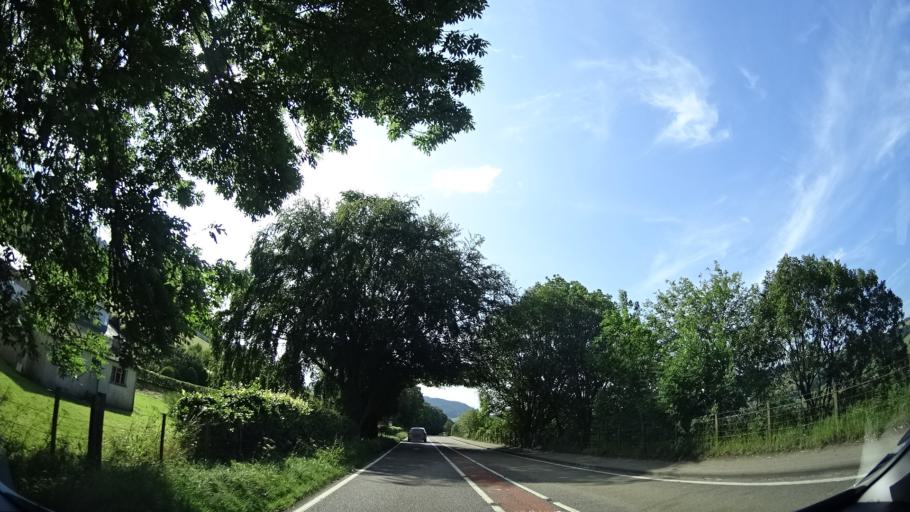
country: GB
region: Scotland
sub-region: Highland
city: Beauly
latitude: 57.3273
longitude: -4.4467
